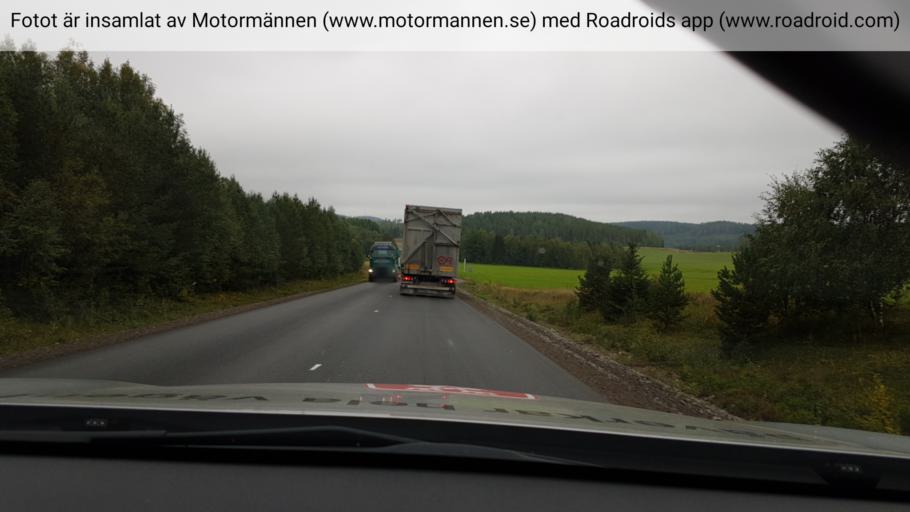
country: SE
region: Vaesterbotten
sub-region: Skelleftea Kommun
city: Burtraesk
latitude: 64.3707
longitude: 20.5034
